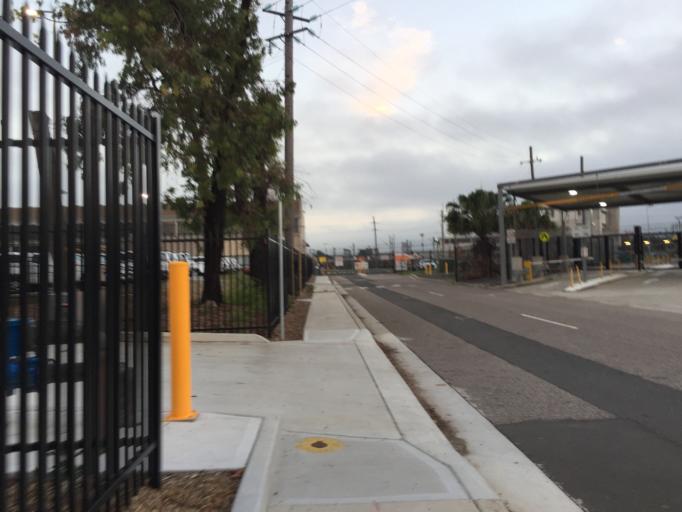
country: AU
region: New South Wales
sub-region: Parramatta
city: Granville
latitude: -33.8399
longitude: 151.0192
